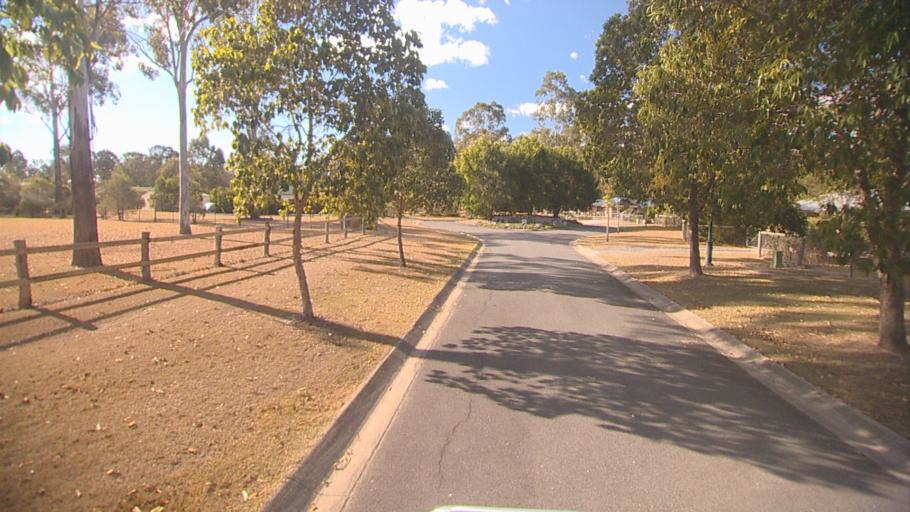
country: AU
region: Queensland
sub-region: Logan
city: North Maclean
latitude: -27.8012
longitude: 152.9703
